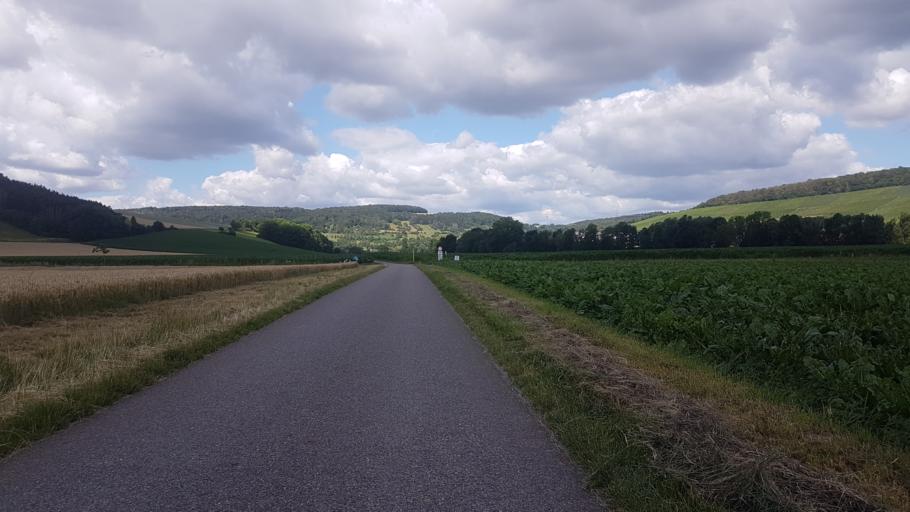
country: DE
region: Bavaria
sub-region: Regierungsbezirk Unterfranken
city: Tauberrettersheim
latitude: 49.4960
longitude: 9.9206
